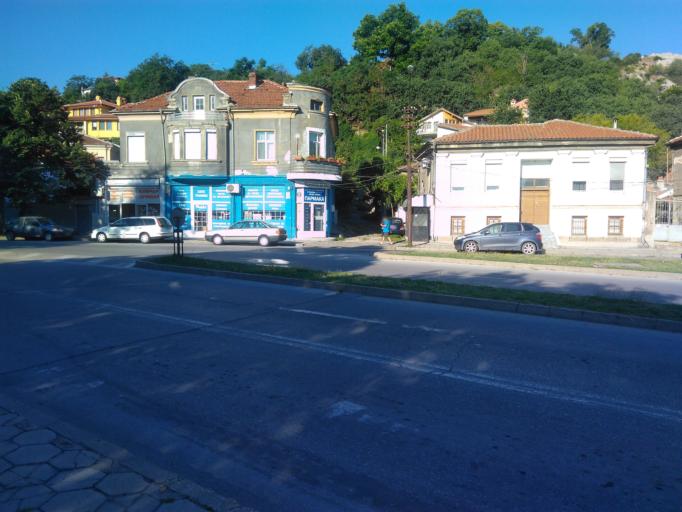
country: BG
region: Plovdiv
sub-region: Obshtina Plovdiv
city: Plovdiv
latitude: 42.1515
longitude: 24.7545
